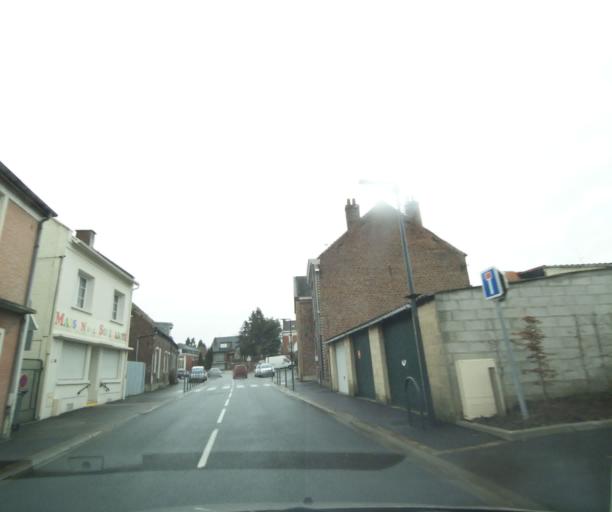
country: FR
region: Nord-Pas-de-Calais
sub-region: Departement du Nord
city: Prouvy
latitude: 50.3172
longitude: 3.4528
